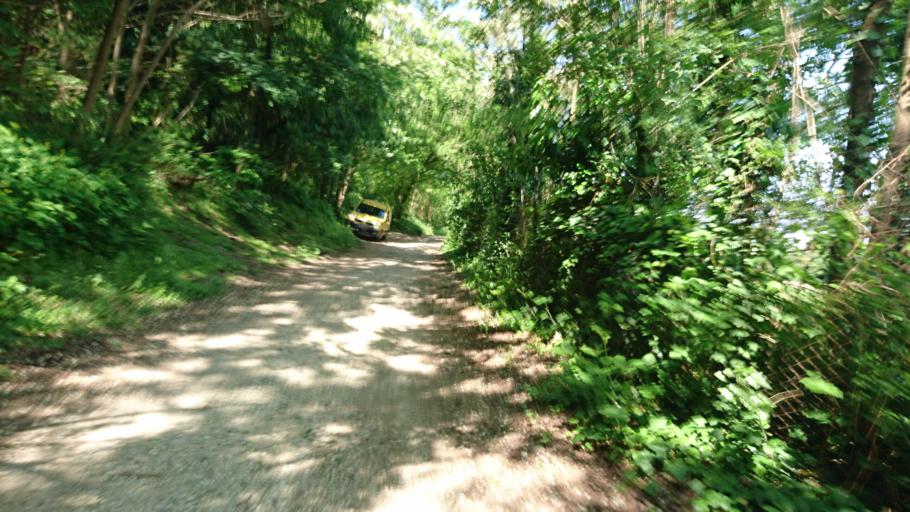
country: IT
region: Veneto
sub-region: Provincia di Padova
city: San Biagio
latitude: 45.3694
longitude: 11.7564
